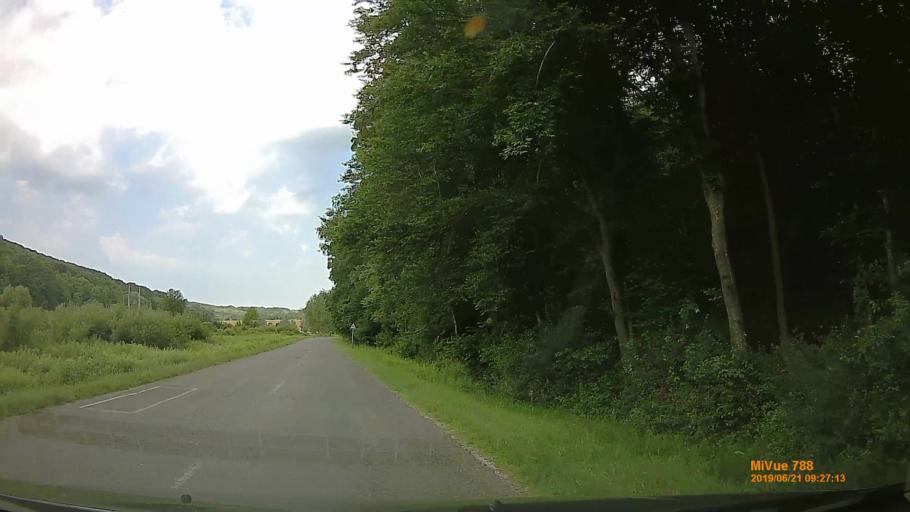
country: HU
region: Somogy
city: Taszar
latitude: 46.2769
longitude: 17.8998
